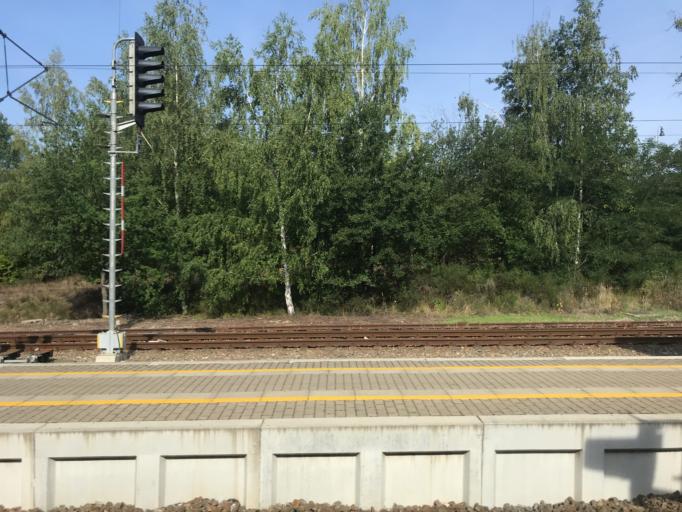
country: CZ
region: Central Bohemia
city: Votice
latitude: 49.6664
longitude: 14.6237
